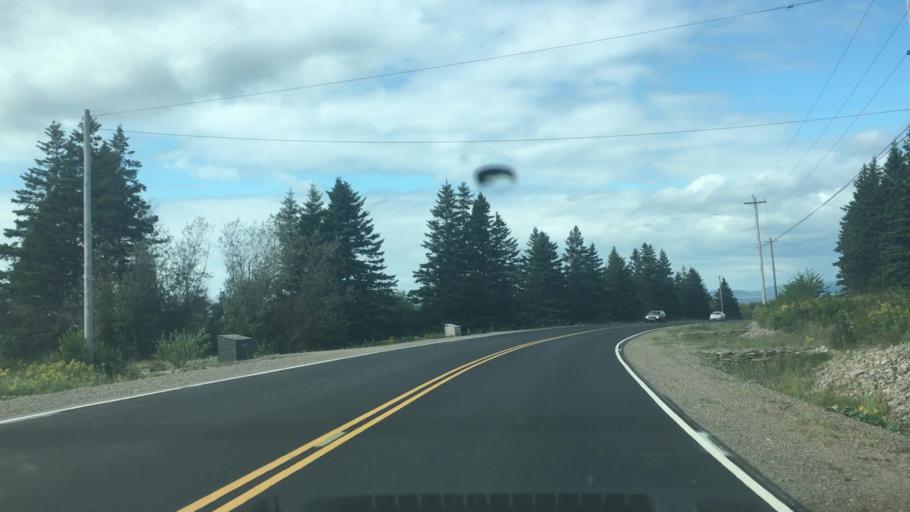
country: CA
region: Nova Scotia
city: Princeville
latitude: 45.7887
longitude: -60.7406
